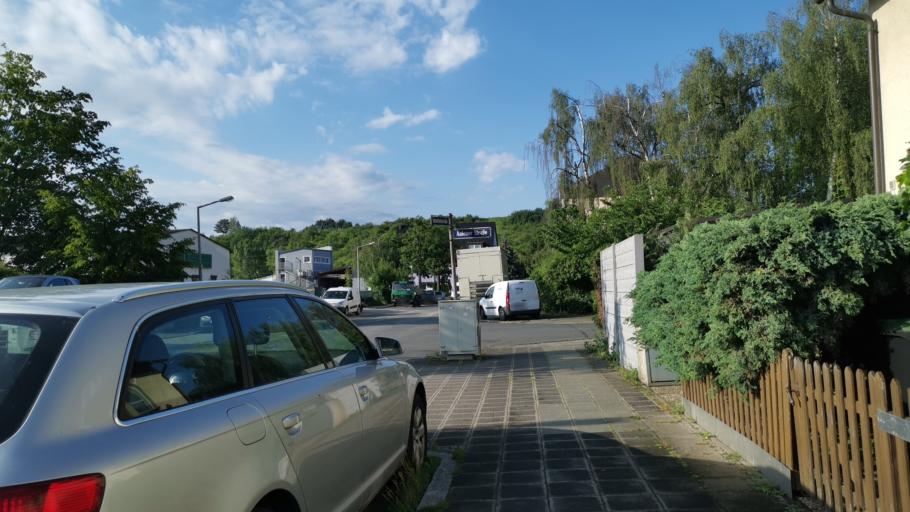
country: DE
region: Bavaria
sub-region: Regierungsbezirk Mittelfranken
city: Grossreuth bei Schweinau
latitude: 49.4248
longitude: 11.0464
